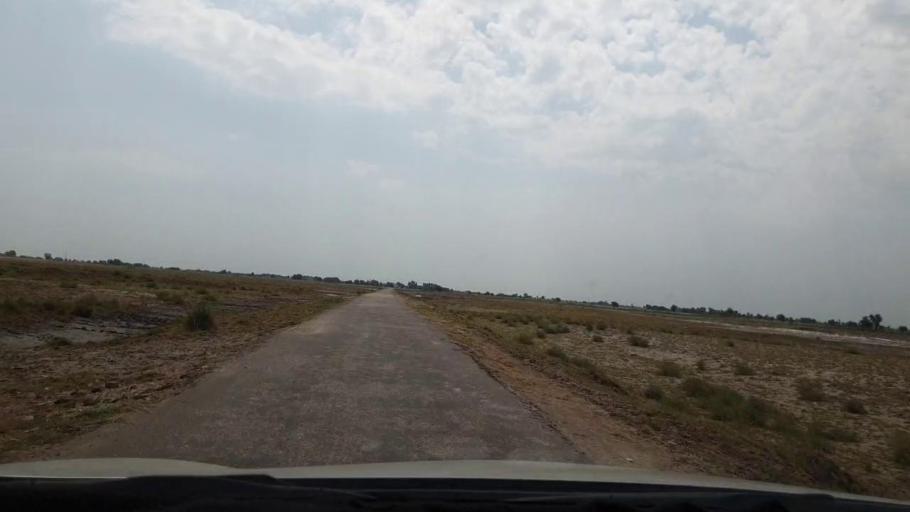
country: PK
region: Sindh
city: Ratodero
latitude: 27.8389
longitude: 68.2994
